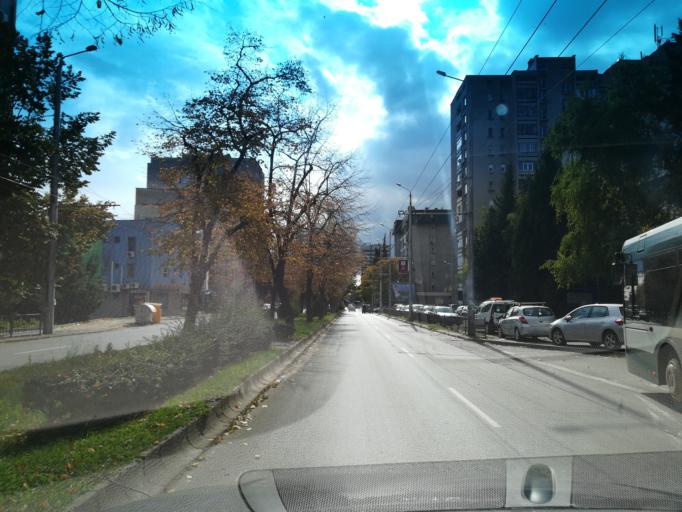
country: BG
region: Stara Zagora
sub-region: Obshtina Stara Zagora
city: Stara Zagora
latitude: 42.4316
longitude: 25.6327
